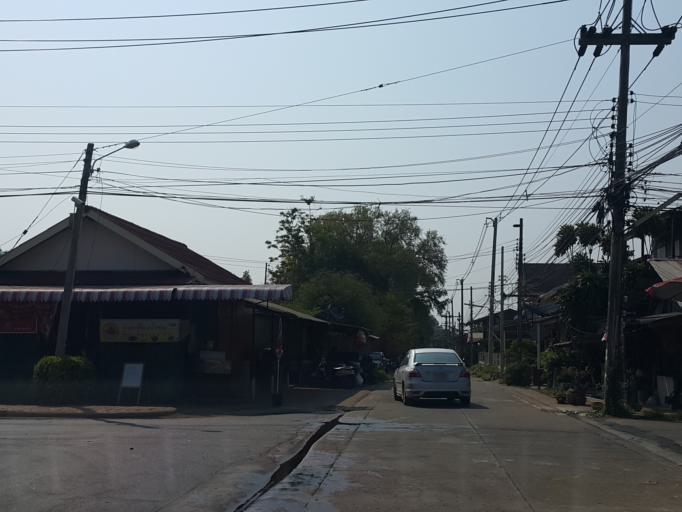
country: TH
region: Kanchanaburi
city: Sai Yok
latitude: 14.1193
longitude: 99.1390
